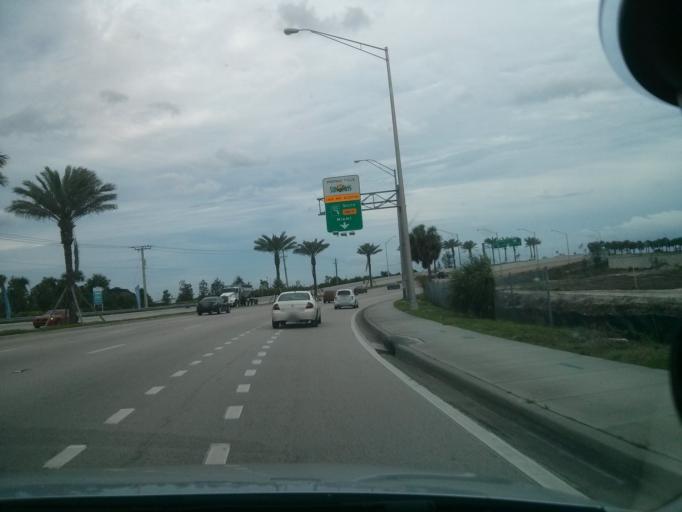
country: US
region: Florida
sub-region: Broward County
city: Palm Aire
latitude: 26.1935
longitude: -80.2138
